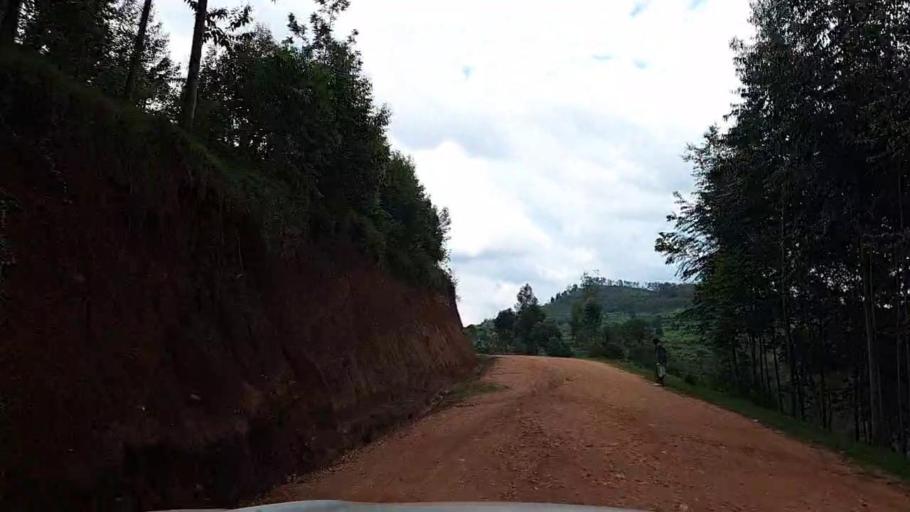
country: RW
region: Southern Province
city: Nyanza
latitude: -2.4105
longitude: 29.6750
